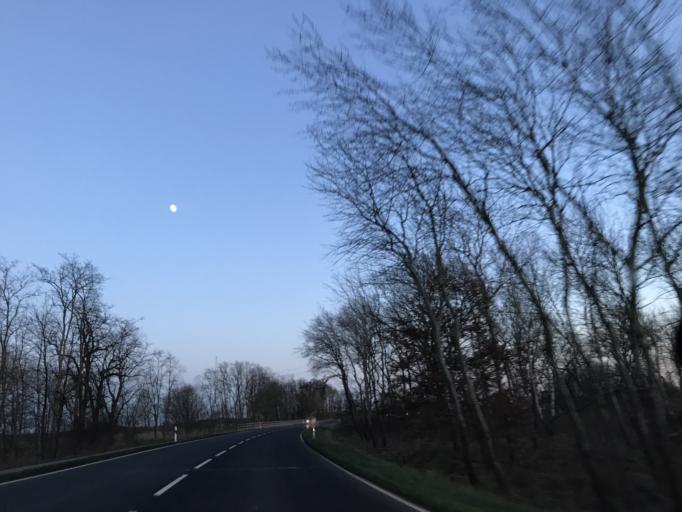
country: DE
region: Brandenburg
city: Premnitz
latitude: 52.5117
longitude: 12.4329
